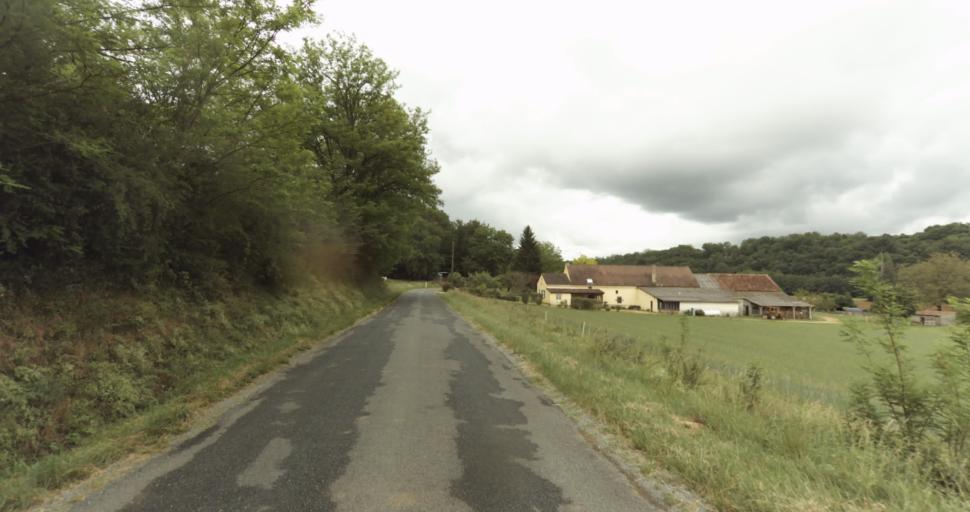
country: FR
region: Aquitaine
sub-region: Departement de la Dordogne
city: Belves
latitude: 44.7596
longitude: 0.8931
